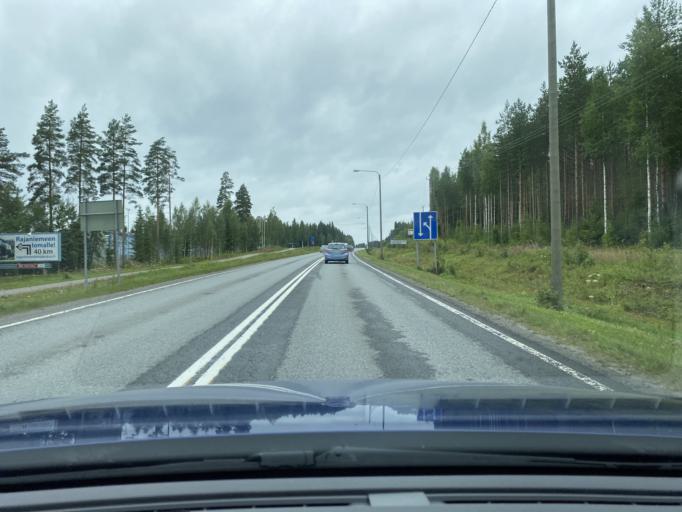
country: FI
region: Central Finland
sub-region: Keuruu
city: Keuruu
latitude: 62.2429
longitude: 24.4804
